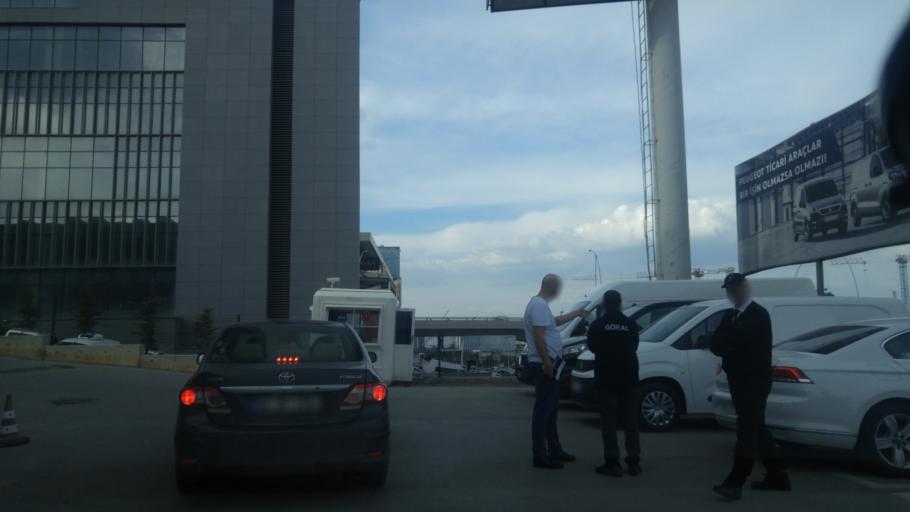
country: TR
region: Ankara
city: Ankara
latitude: 39.8861
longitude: 32.8118
